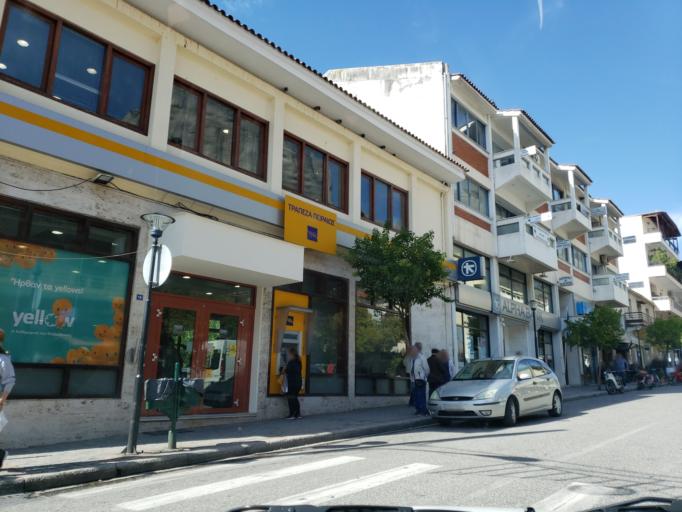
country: GR
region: Thessaly
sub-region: Trikala
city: Kalampaka
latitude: 39.7062
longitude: 21.6248
